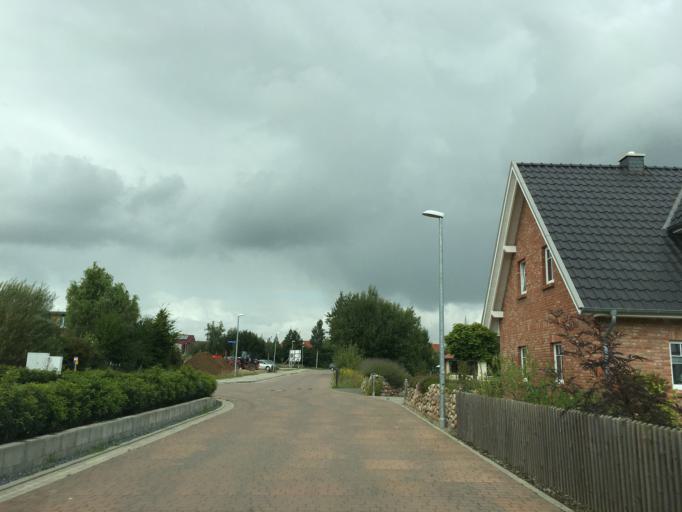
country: DE
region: Lower Saxony
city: Melbeck
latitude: 53.2086
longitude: 10.3788
